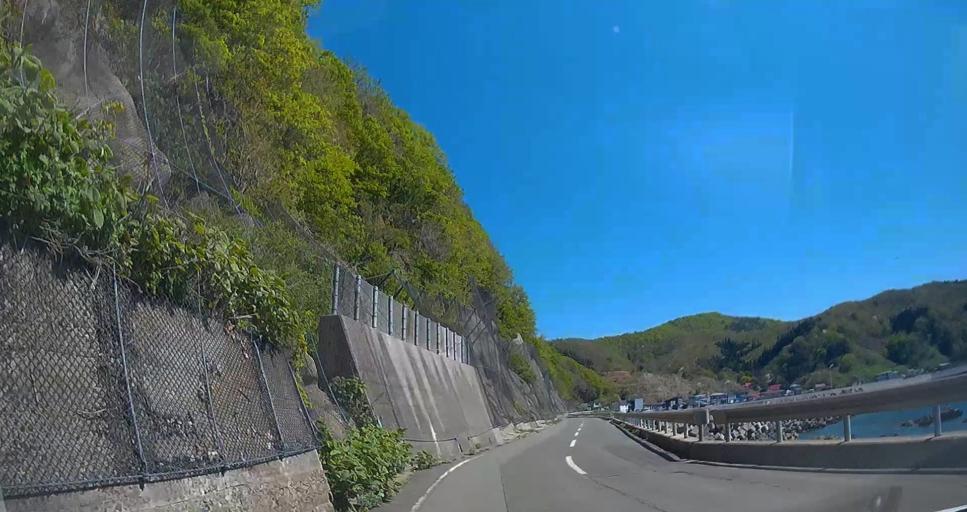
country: JP
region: Aomori
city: Aomori Shi
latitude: 41.1321
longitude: 140.7882
